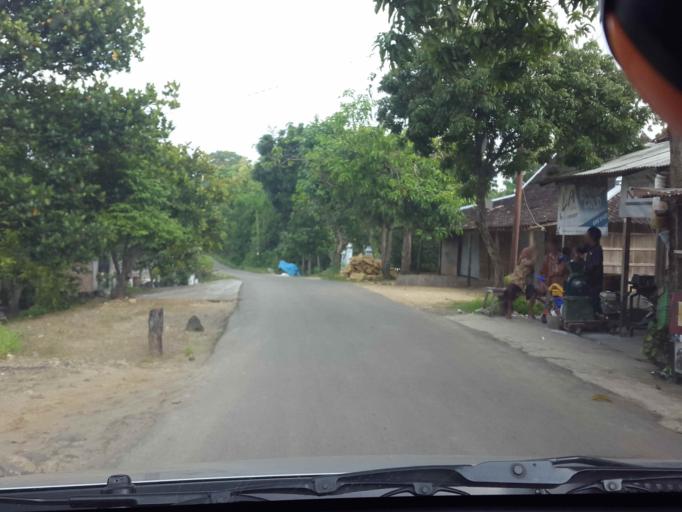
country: ID
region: Central Java
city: Sragen
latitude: -7.2989
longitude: 110.9127
